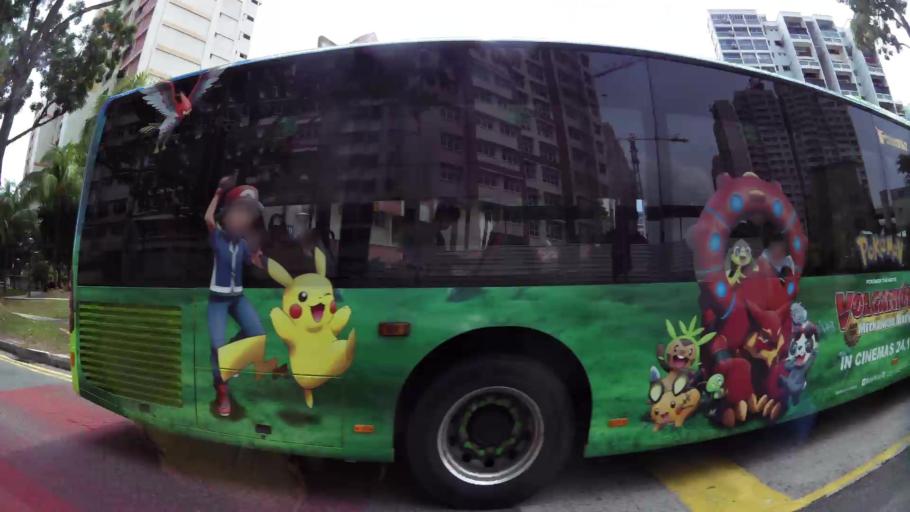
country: MY
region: Johor
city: Johor Bahru
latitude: 1.3517
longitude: 103.7438
